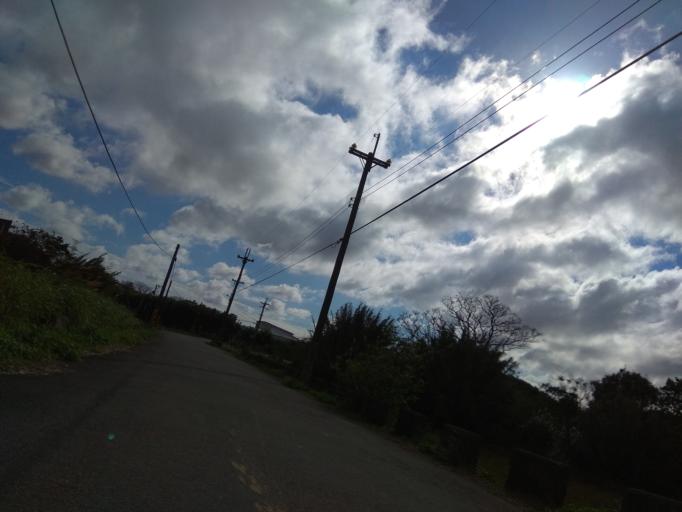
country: TW
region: Taiwan
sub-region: Hsinchu
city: Zhubei
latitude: 24.9706
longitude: 121.0861
